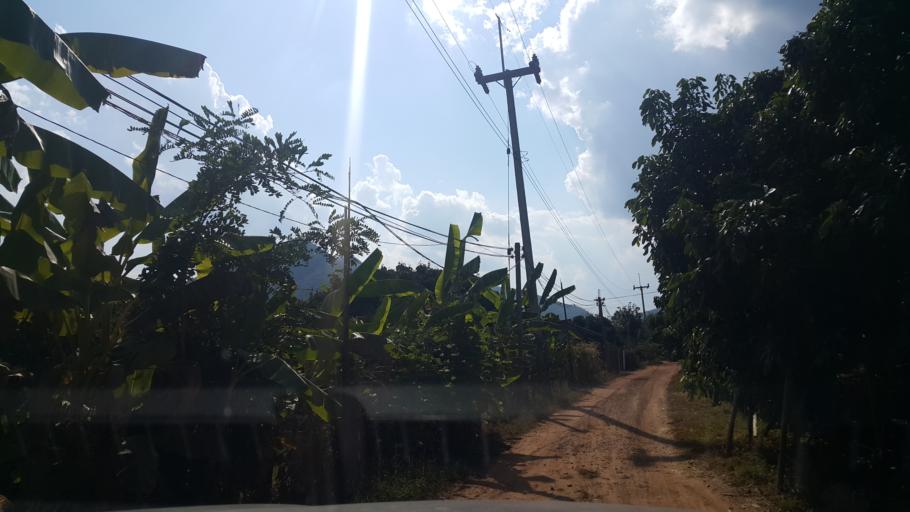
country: TH
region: Lamphun
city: Ban Thi
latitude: 18.5958
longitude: 99.1566
